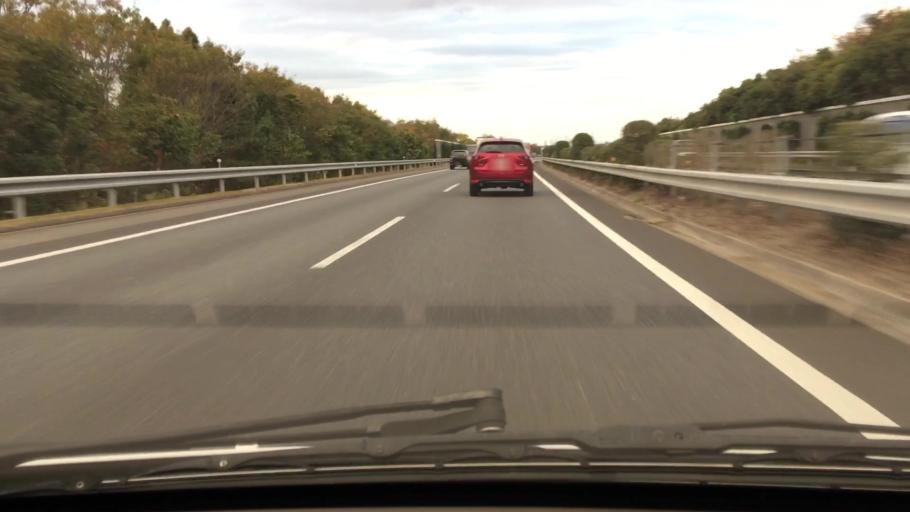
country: JP
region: Chiba
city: Ichihara
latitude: 35.4737
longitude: 140.0826
